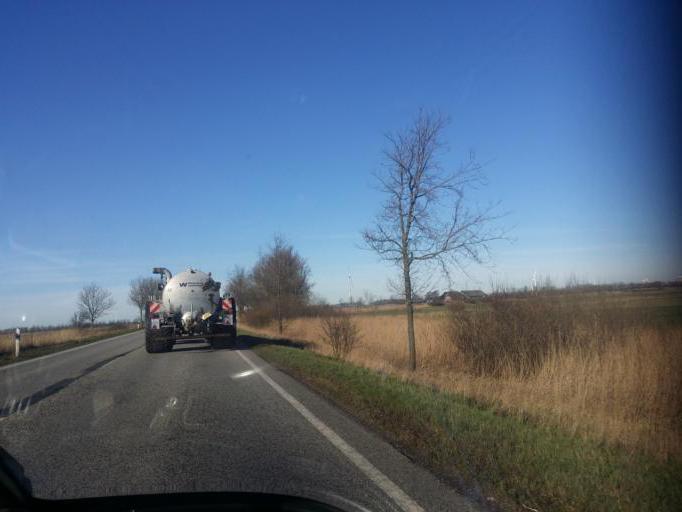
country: DE
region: Schleswig-Holstein
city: Husum
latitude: 54.4348
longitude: 9.0468
